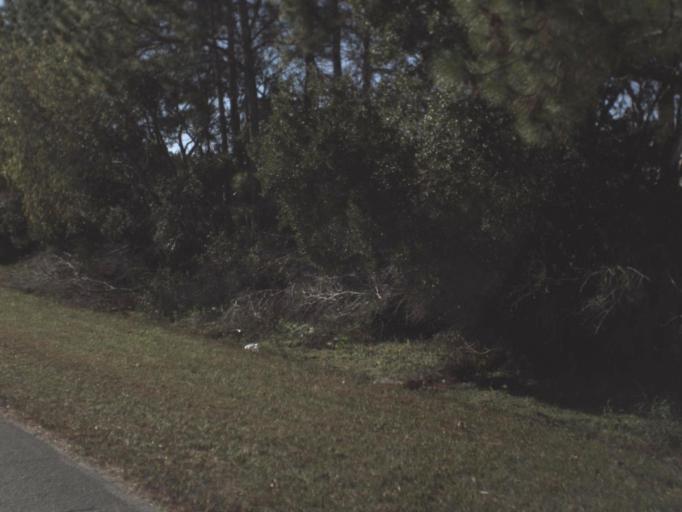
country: US
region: Florida
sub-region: Volusia County
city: Daytona Beach
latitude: 29.1779
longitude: -81.0765
